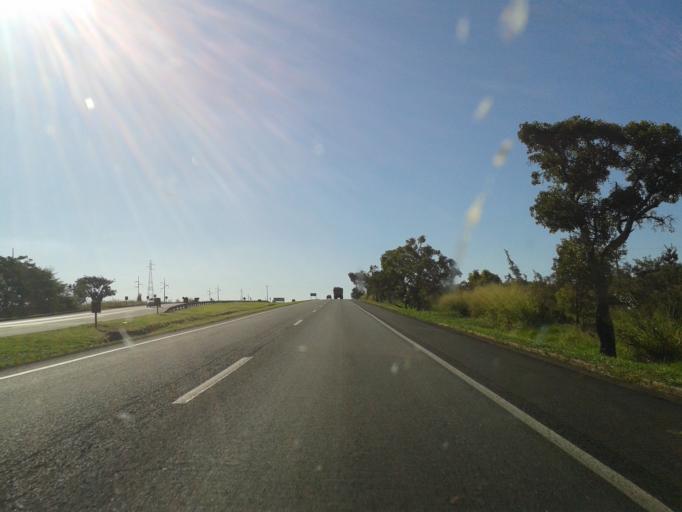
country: BR
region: Minas Gerais
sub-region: Uberlandia
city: Uberlandia
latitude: -19.0829
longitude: -48.1865
